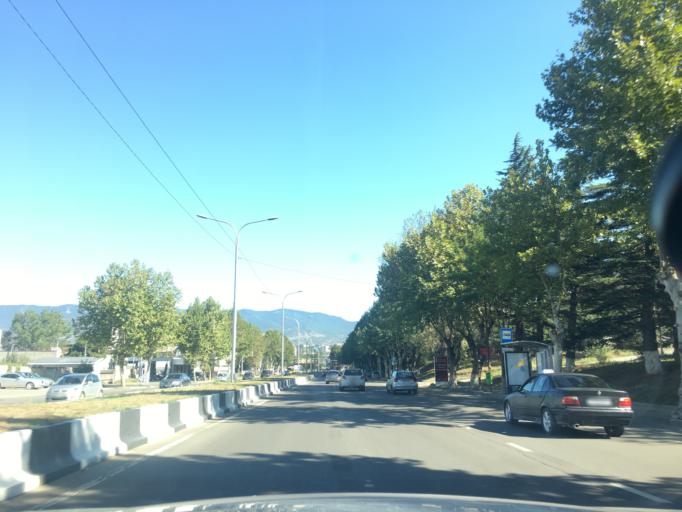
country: GE
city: Zahesi
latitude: 41.7801
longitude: 44.7966
